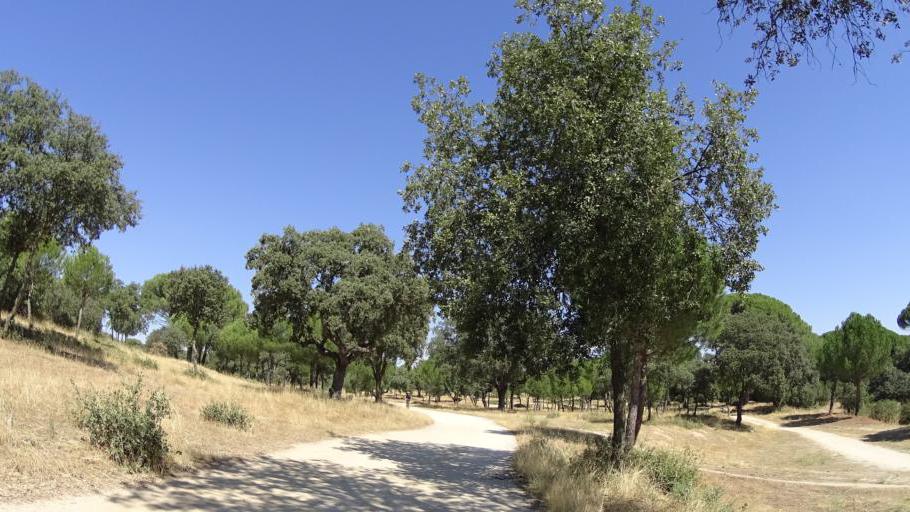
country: ES
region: Madrid
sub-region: Provincia de Madrid
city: Boadilla del Monte
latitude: 40.4252
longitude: -3.8539
